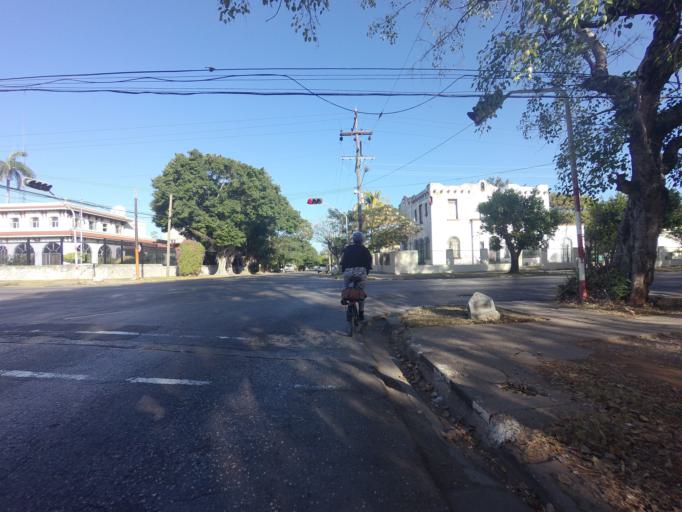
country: CU
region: La Habana
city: Havana
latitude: 23.1177
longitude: -82.4231
